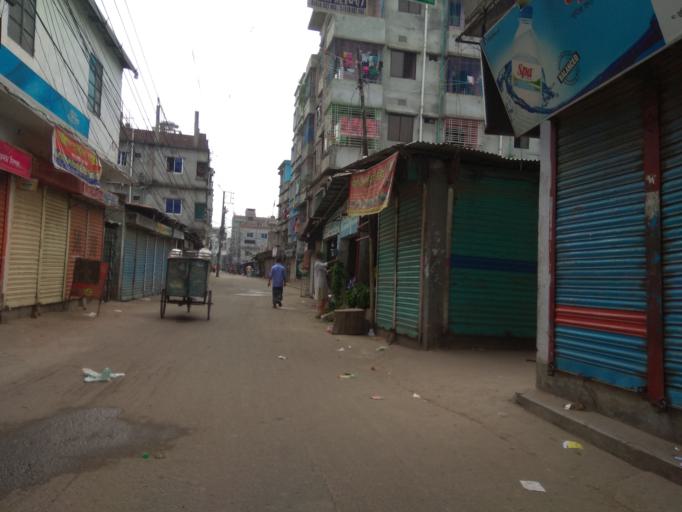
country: BD
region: Dhaka
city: Azimpur
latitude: 23.7160
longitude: 90.3628
